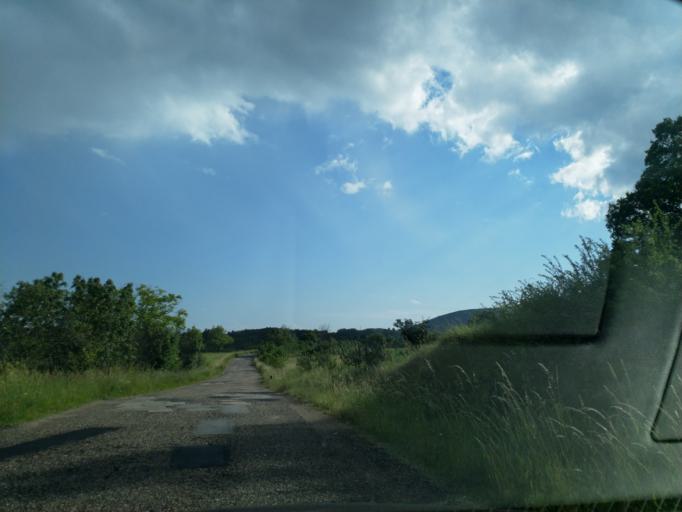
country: RS
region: Central Serbia
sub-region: Zajecarski Okrug
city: Boljevac
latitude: 43.9736
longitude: 21.9715
